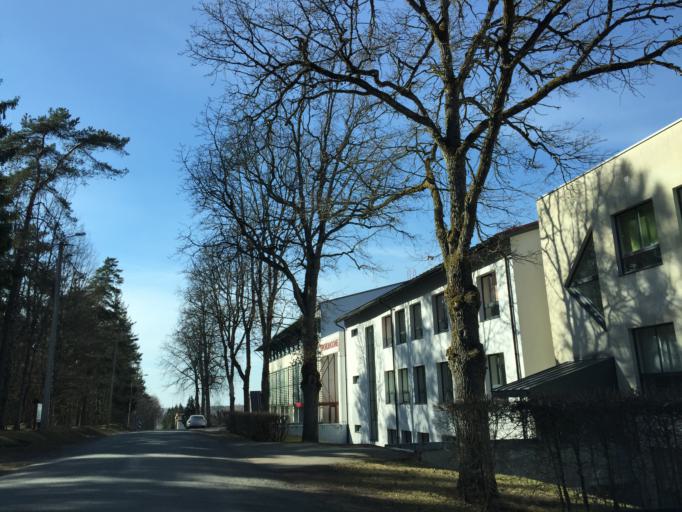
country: EE
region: Tartu
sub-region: Elva linn
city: Elva
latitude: 58.0527
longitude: 26.4946
